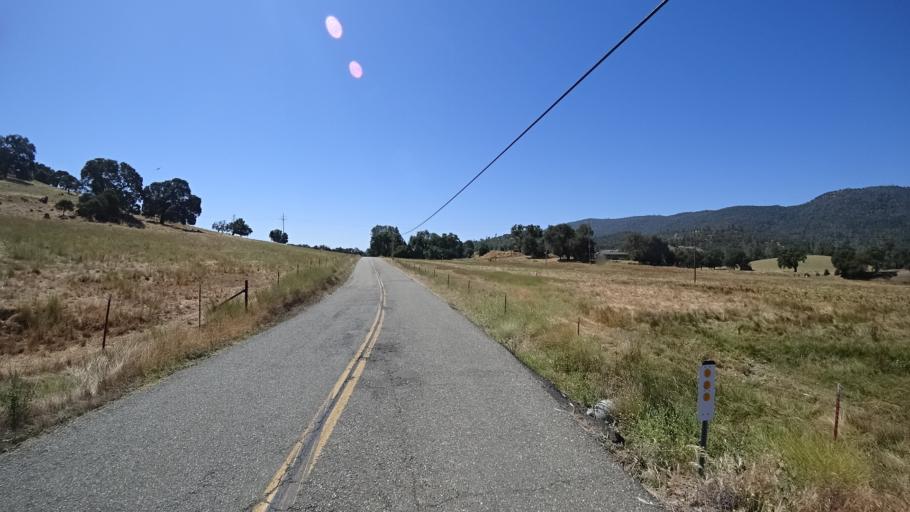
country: US
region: California
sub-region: Calaveras County
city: San Andreas
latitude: 38.1862
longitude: -120.6829
